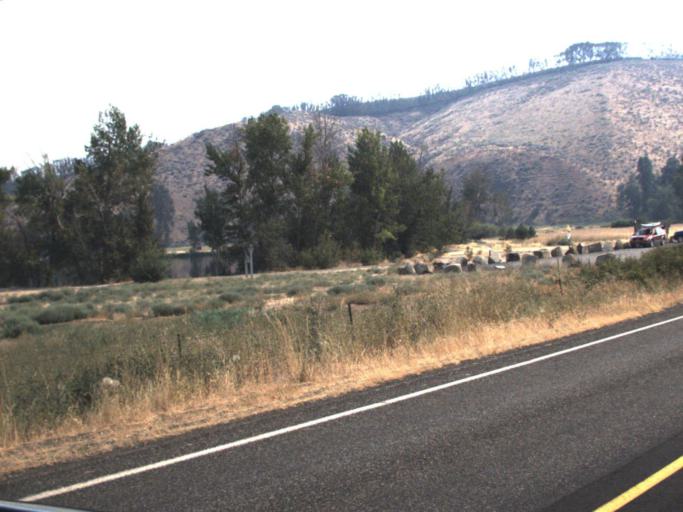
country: US
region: Washington
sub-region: Kittitas County
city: Ellensburg
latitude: 46.9254
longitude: -120.5099
